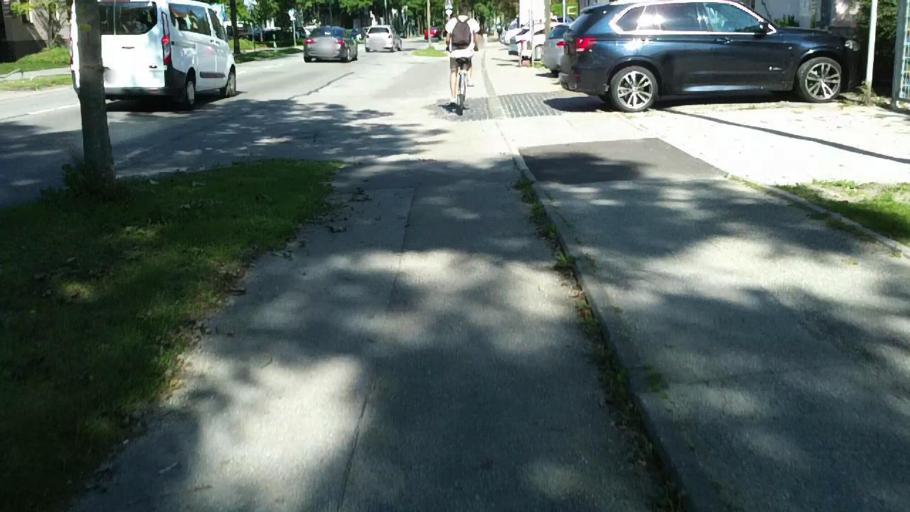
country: DE
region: Bavaria
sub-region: Upper Bavaria
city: Karlsfeld
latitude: 48.1859
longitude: 11.5043
